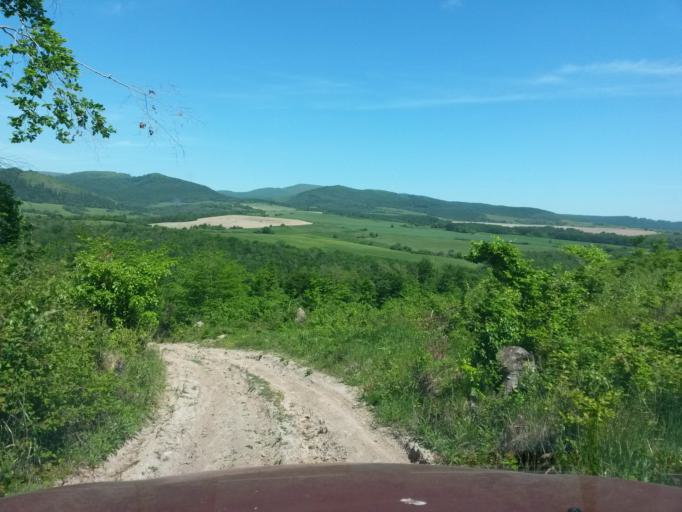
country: SK
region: Presovsky
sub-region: Okres Presov
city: Presov
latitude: 48.8794
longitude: 21.3912
